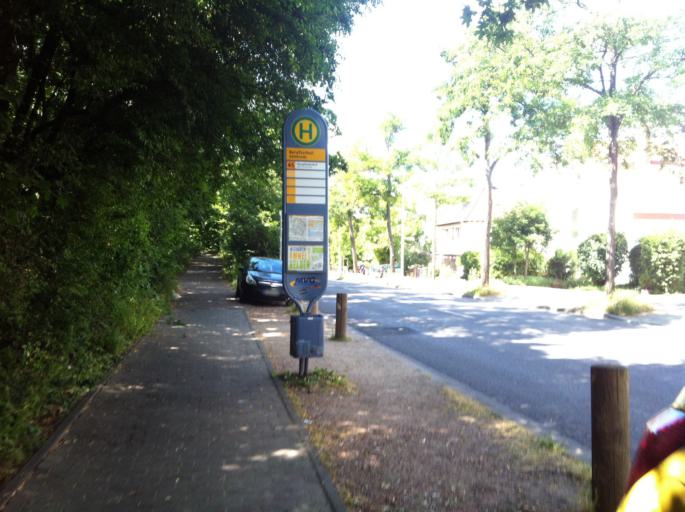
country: DE
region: Rheinland-Pfalz
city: Mainz
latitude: 50.0063
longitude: 8.2459
